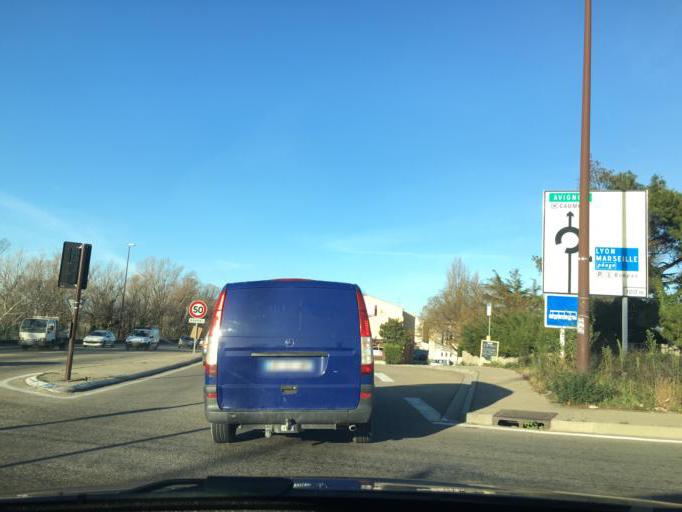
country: FR
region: Provence-Alpes-Cote d'Azur
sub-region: Departement des Bouches-du-Rhone
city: Noves
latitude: 43.8893
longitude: 4.9160
